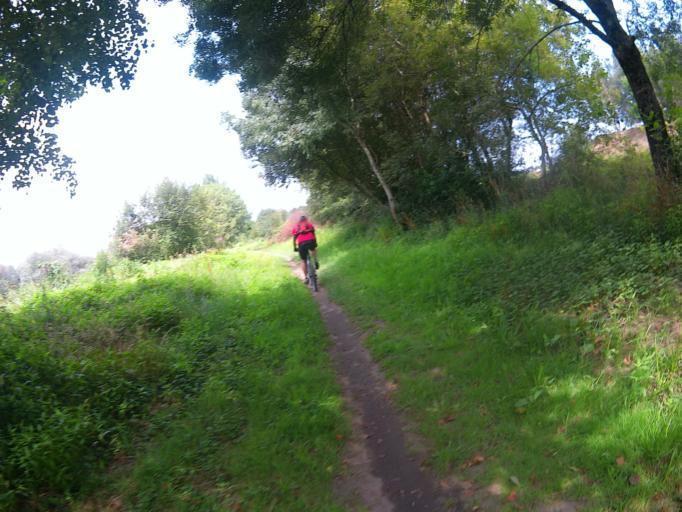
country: PT
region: Viana do Castelo
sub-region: Ponte de Lima
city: Ponte de Lima
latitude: 41.7788
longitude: -8.5740
